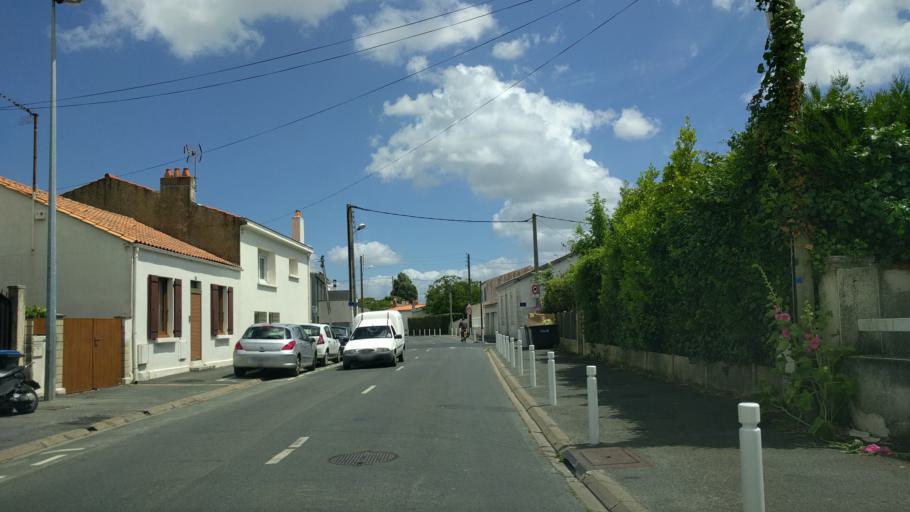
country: FR
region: Poitou-Charentes
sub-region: Departement de la Charente-Maritime
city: La Rochelle
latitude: 46.1611
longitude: -1.1359
